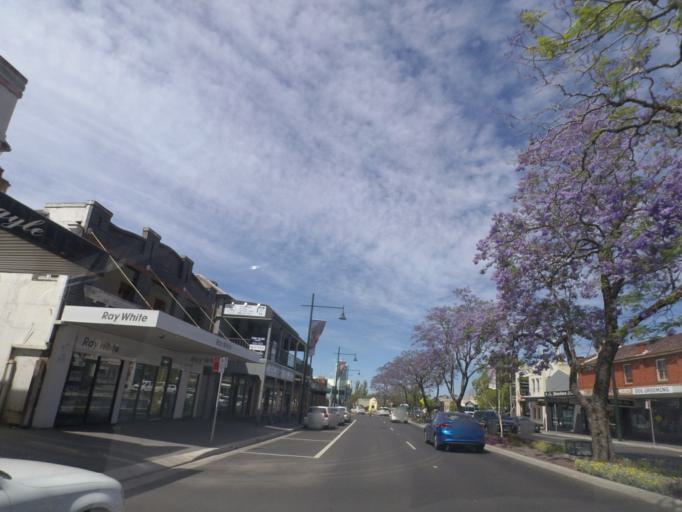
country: AU
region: New South Wales
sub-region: Camden
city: Elderslie
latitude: -34.0541
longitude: 150.6970
